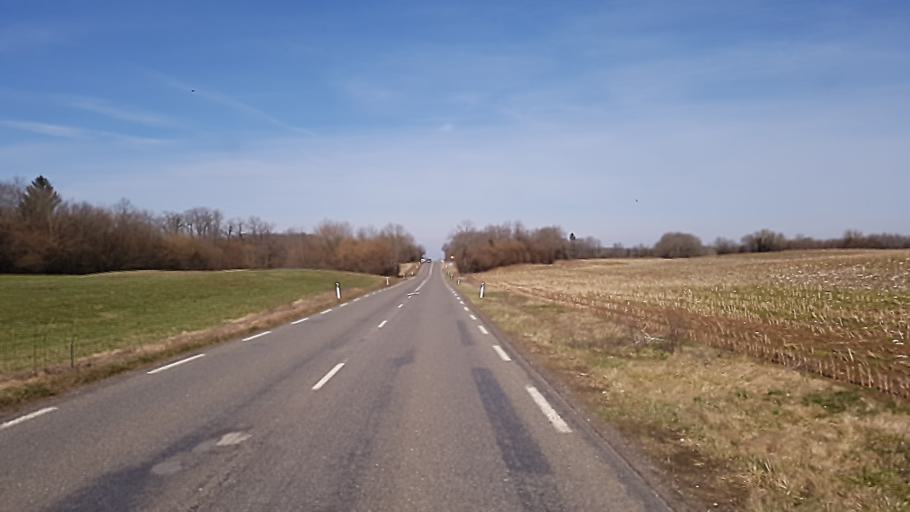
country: FR
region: Franche-Comte
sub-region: Departement du Jura
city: Champagnole
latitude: 46.7864
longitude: 5.8528
